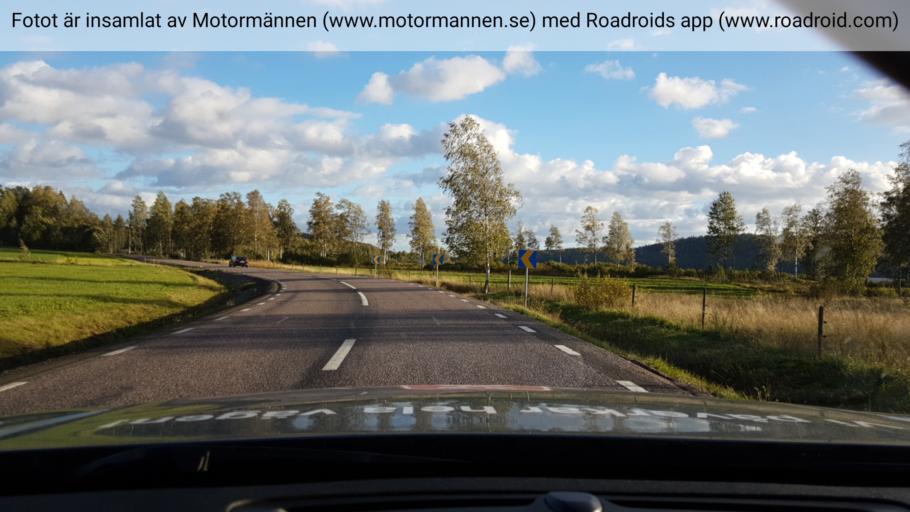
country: SE
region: Vaermland
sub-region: Karlstads Kommun
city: Molkom
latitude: 59.6790
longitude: 13.6800
